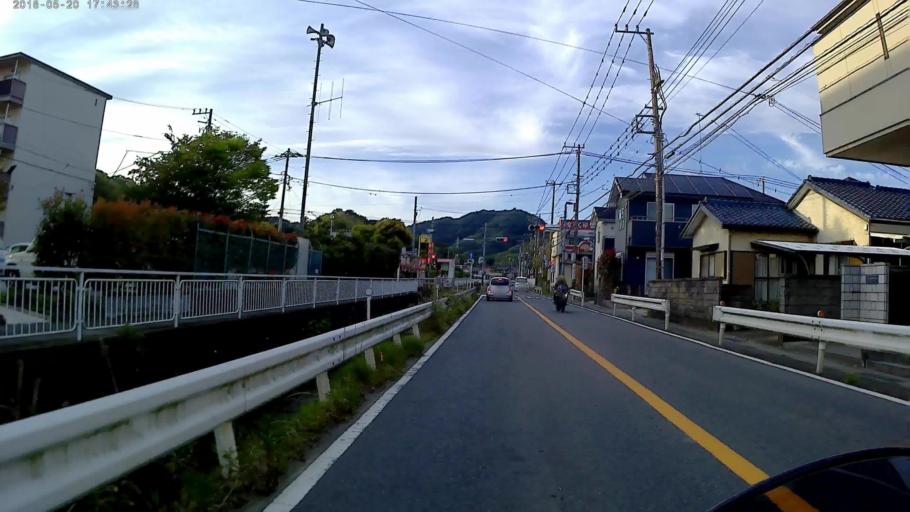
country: JP
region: Kanagawa
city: Ninomiya
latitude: 35.3142
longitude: 139.2778
